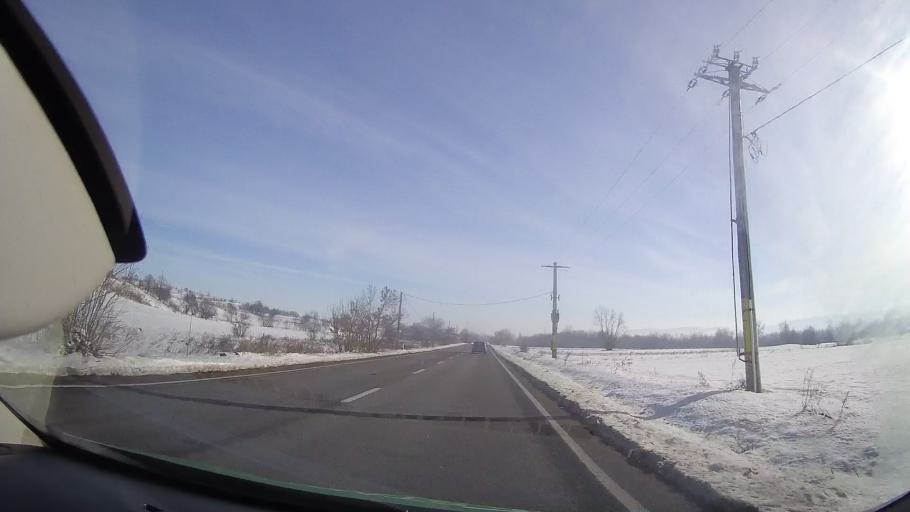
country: RO
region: Neamt
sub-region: Comuna Ghindaoani
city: Ghindaoani
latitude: 47.0774
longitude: 26.3510
